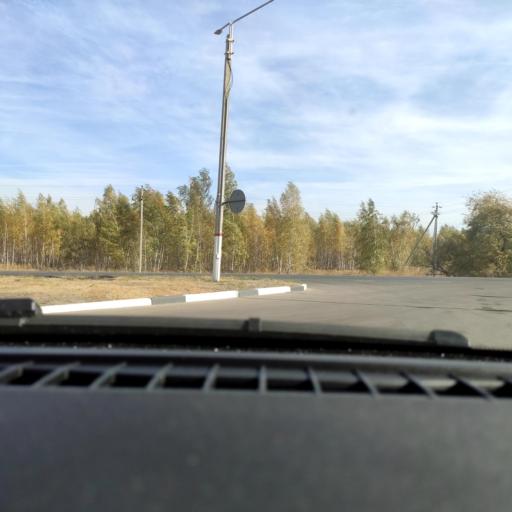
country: RU
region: Voronezj
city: Maslovka
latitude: 51.5864
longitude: 39.2548
